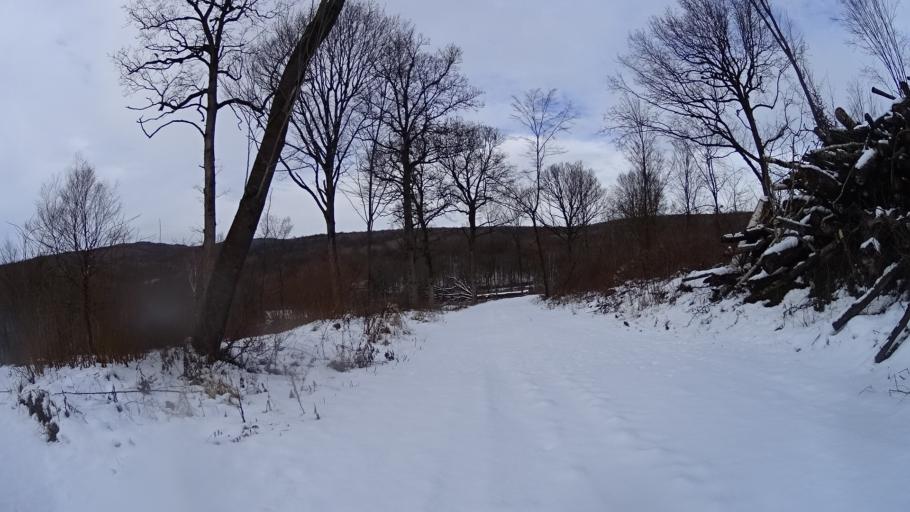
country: AT
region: Lower Austria
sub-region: Politischer Bezirk Korneuburg
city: Leobendorf
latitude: 48.4116
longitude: 16.3192
